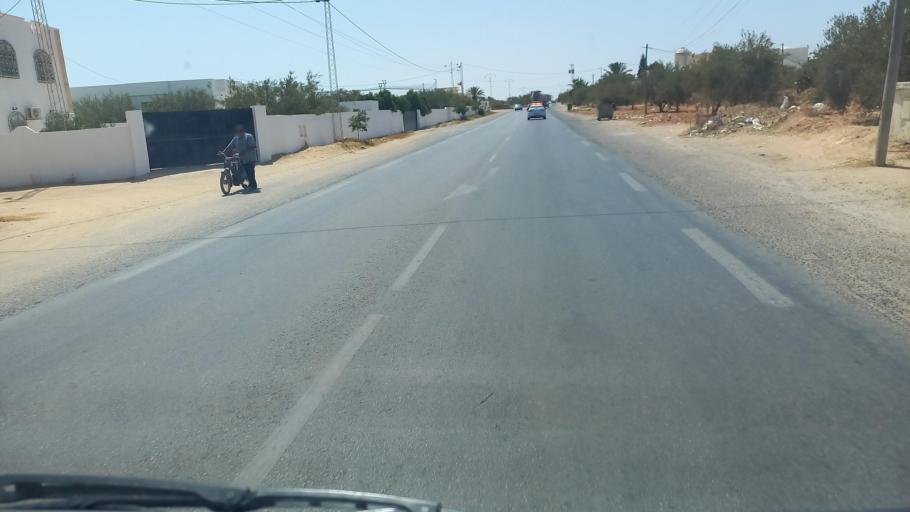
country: TN
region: Madanin
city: Houmt Souk
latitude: 33.7919
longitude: 10.8874
